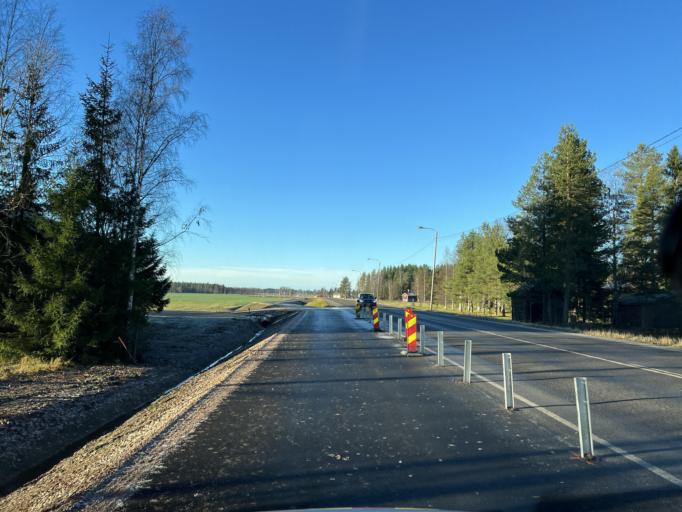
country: FI
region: Northern Ostrobothnia
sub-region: Nivala-Haapajaervi
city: Nivala
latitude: 63.9508
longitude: 24.9133
